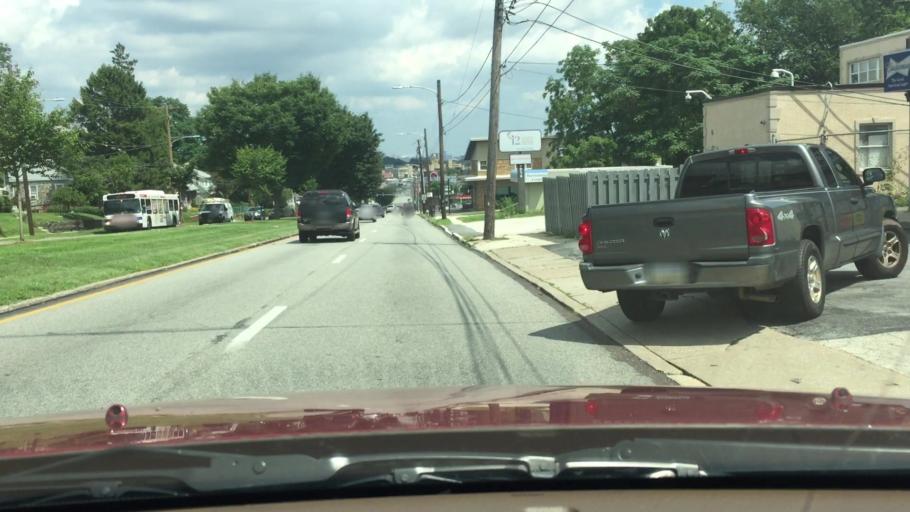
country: US
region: Pennsylvania
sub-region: Montgomery County
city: Penn Wynne
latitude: 39.9645
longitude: -75.2738
